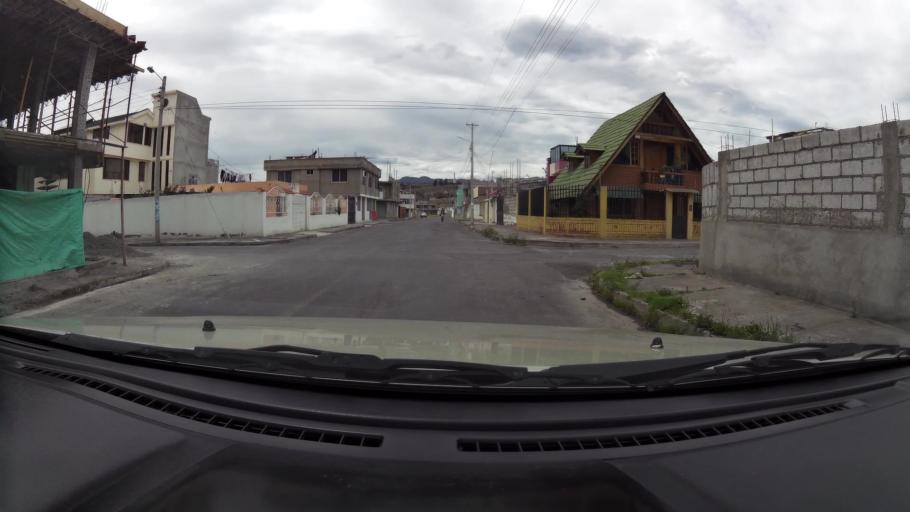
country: EC
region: Cotopaxi
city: Latacunga
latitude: -0.9530
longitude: -78.6030
